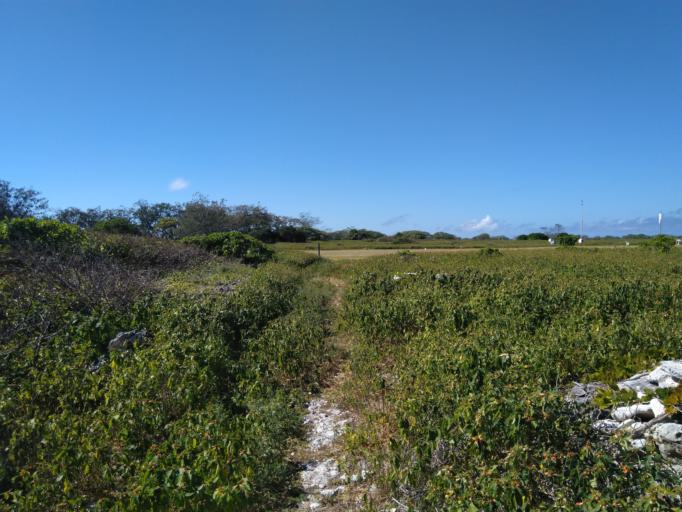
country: AU
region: Queensland
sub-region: Bundaberg
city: Bundaberg
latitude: -24.1110
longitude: 152.7150
